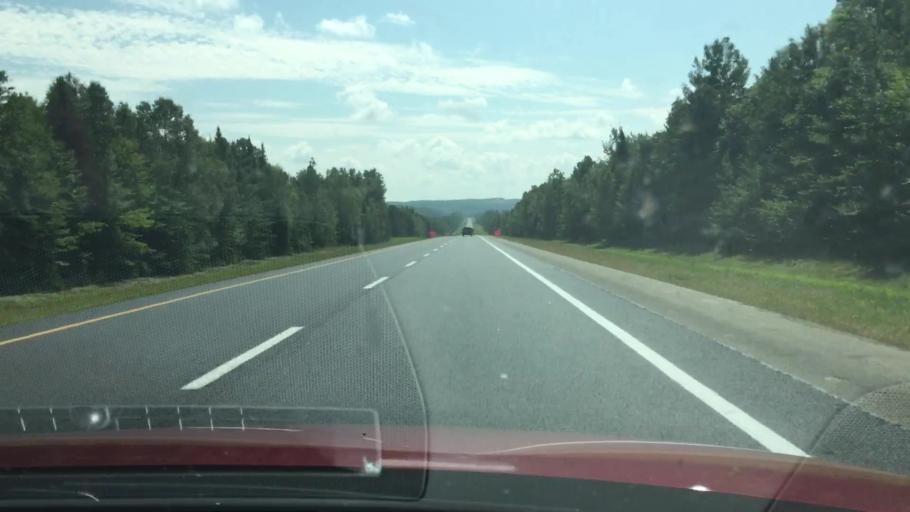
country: US
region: Maine
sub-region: Penobscot County
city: Patten
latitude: 45.8335
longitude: -68.4335
